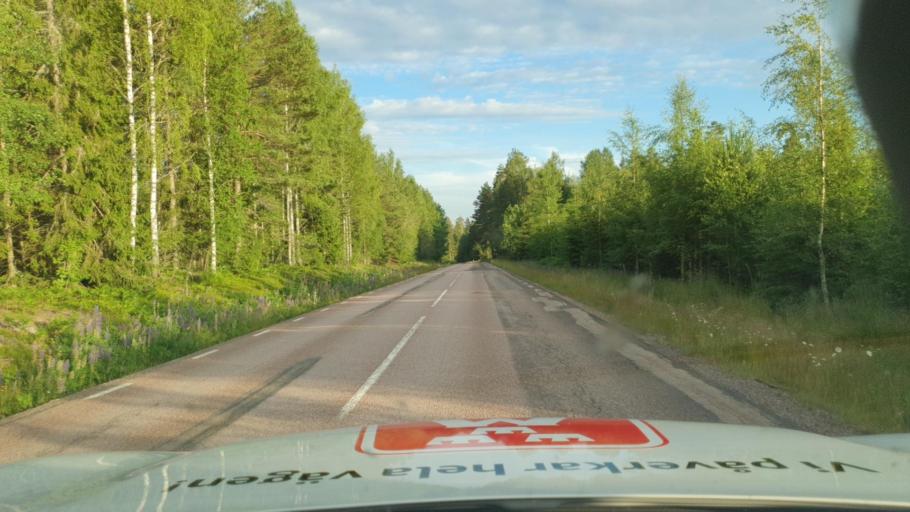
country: SE
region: Vaermland
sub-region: Karlstads Kommun
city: Molkom
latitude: 59.5136
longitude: 13.7946
